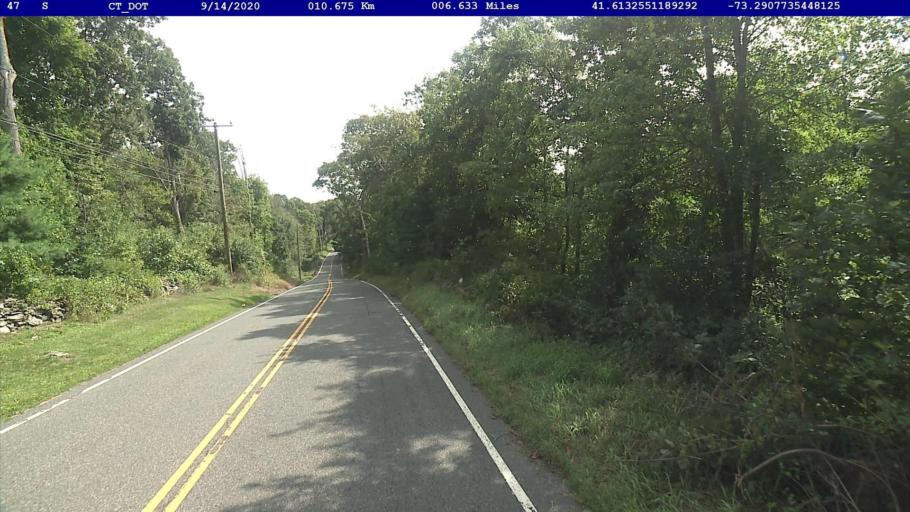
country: US
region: Connecticut
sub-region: Litchfield County
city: New Preston
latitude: 41.6133
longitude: -73.2908
